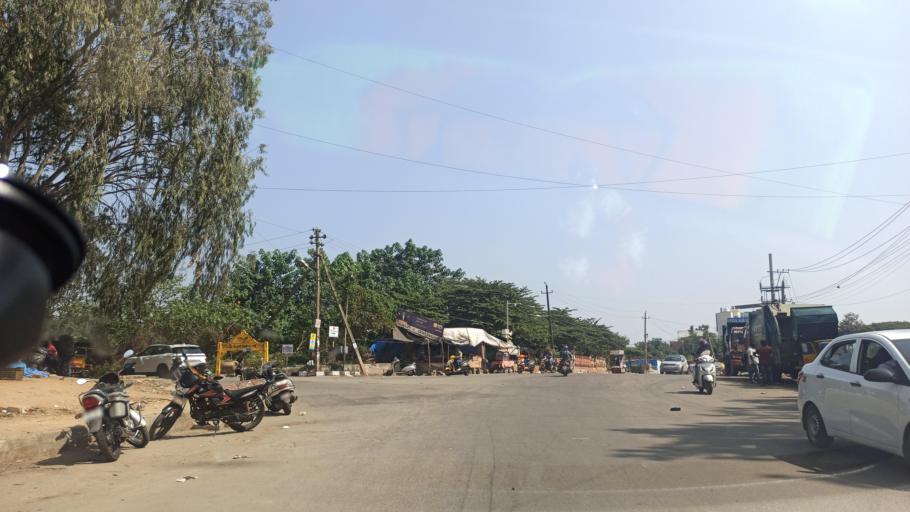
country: IN
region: Karnataka
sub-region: Bangalore Urban
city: Yelahanka
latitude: 13.0558
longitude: 77.5976
